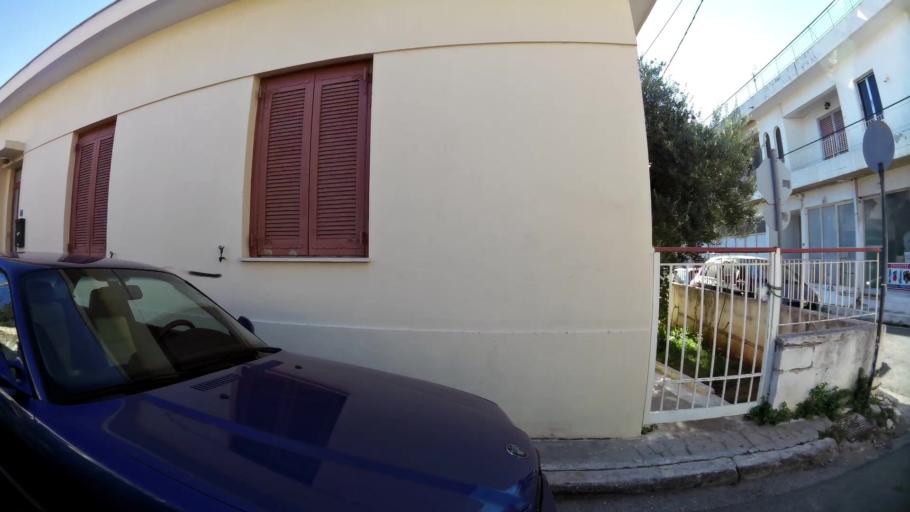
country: GR
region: Attica
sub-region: Nomarchia Anatolikis Attikis
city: Koropi
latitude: 37.8983
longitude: 23.8730
